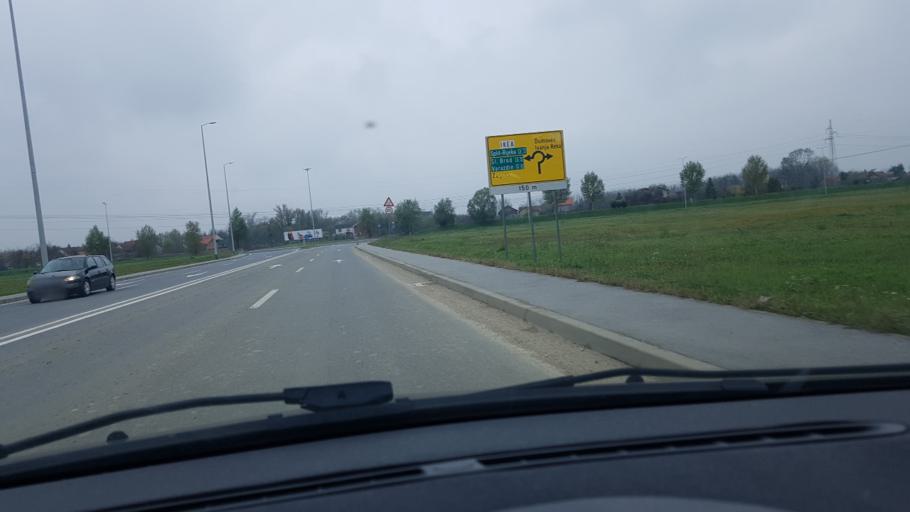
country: HR
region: Grad Zagreb
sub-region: Sesvete
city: Sesvete
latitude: 45.7943
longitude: 16.1478
